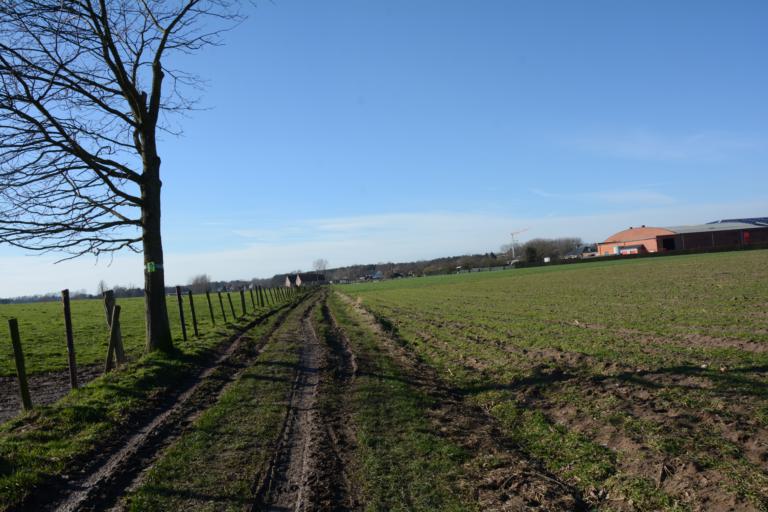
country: BE
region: Flanders
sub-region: Provincie Oost-Vlaanderen
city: Beveren
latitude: 51.1750
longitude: 4.2286
